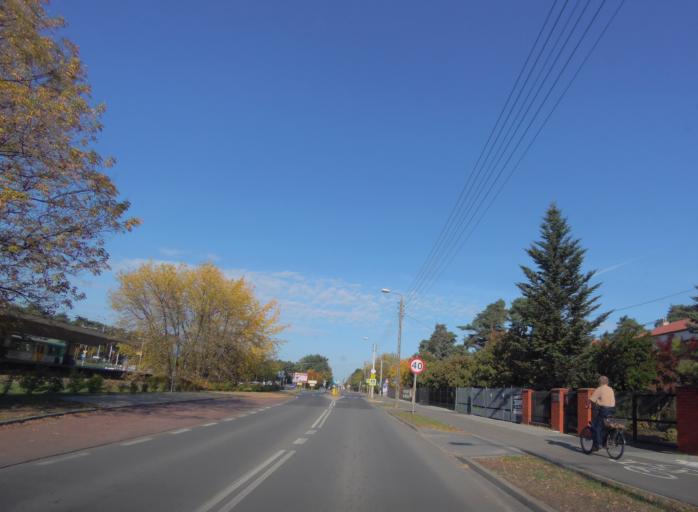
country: PL
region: Masovian Voivodeship
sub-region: Powiat otwocki
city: Jozefow
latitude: 52.1483
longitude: 21.2250
